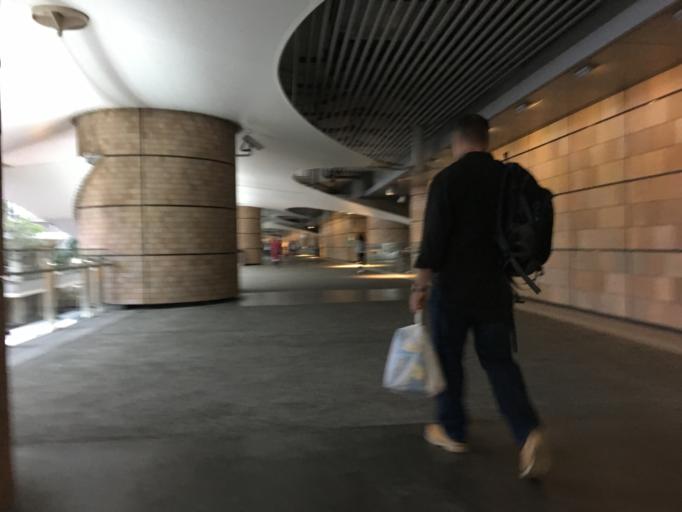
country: HK
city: Tai O
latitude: 22.2914
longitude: 113.9456
